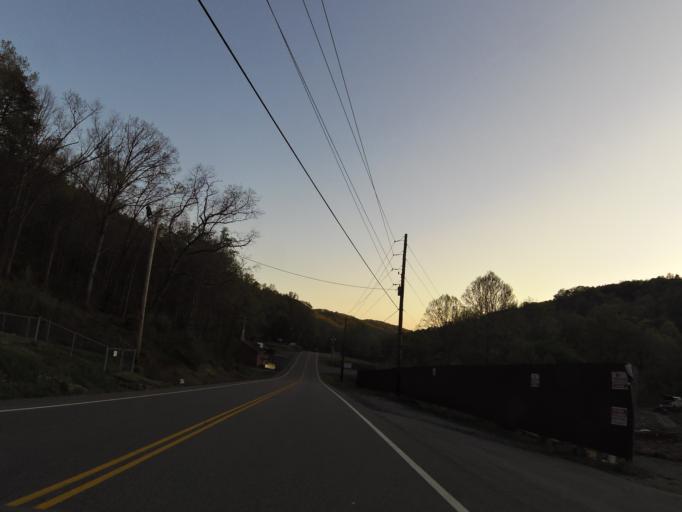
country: US
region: Tennessee
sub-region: Campbell County
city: Fincastle
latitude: 36.4288
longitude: -84.0835
